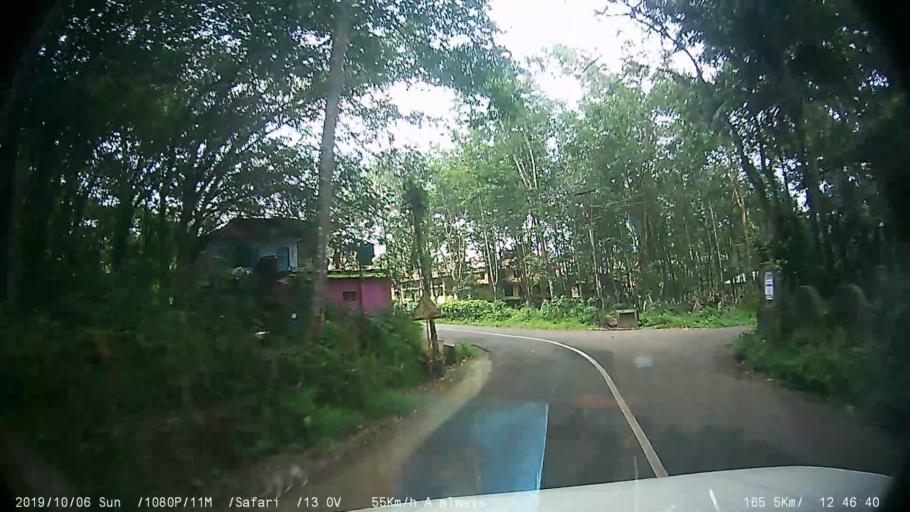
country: IN
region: Kerala
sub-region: Kottayam
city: Palackattumala
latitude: 9.7720
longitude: 76.6060
